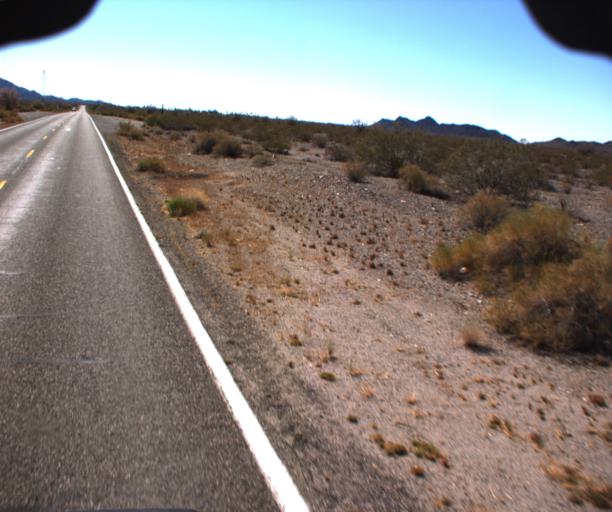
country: US
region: Arizona
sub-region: La Paz County
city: Salome
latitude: 33.7306
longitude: -113.7190
